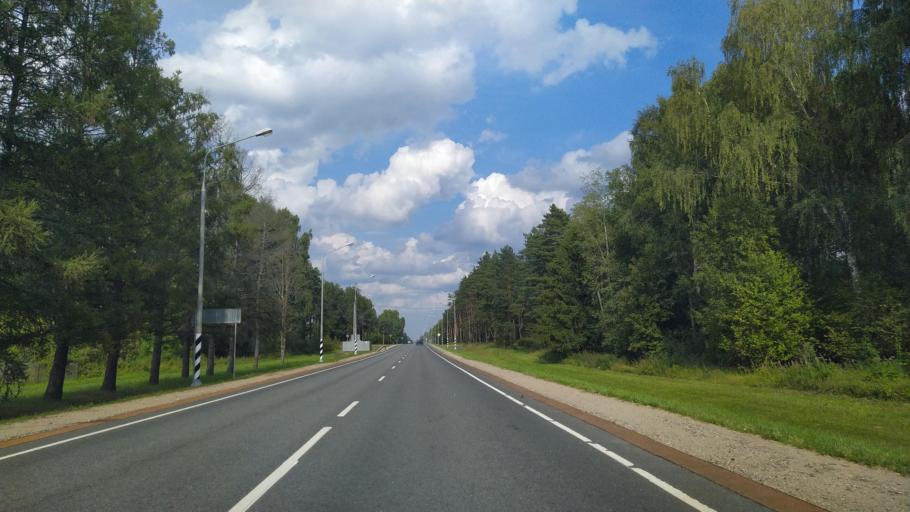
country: RU
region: Novgorod
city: Shimsk
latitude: 58.1782
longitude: 30.5318
